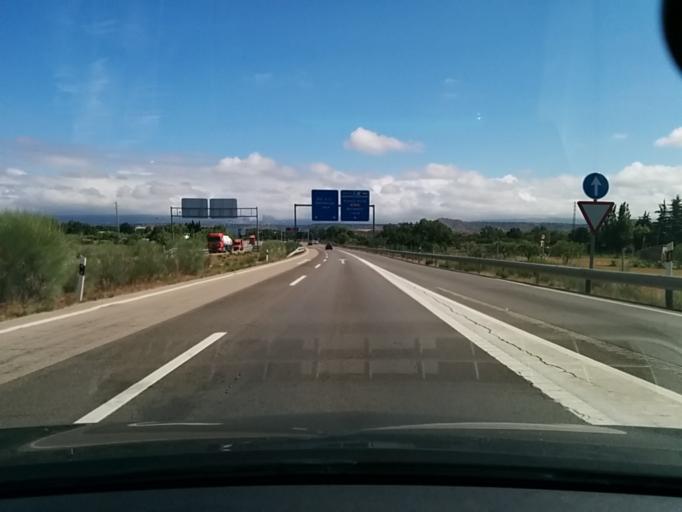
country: ES
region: Aragon
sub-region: Provincia de Huesca
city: Huesca
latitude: 42.1513
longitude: -0.4246
